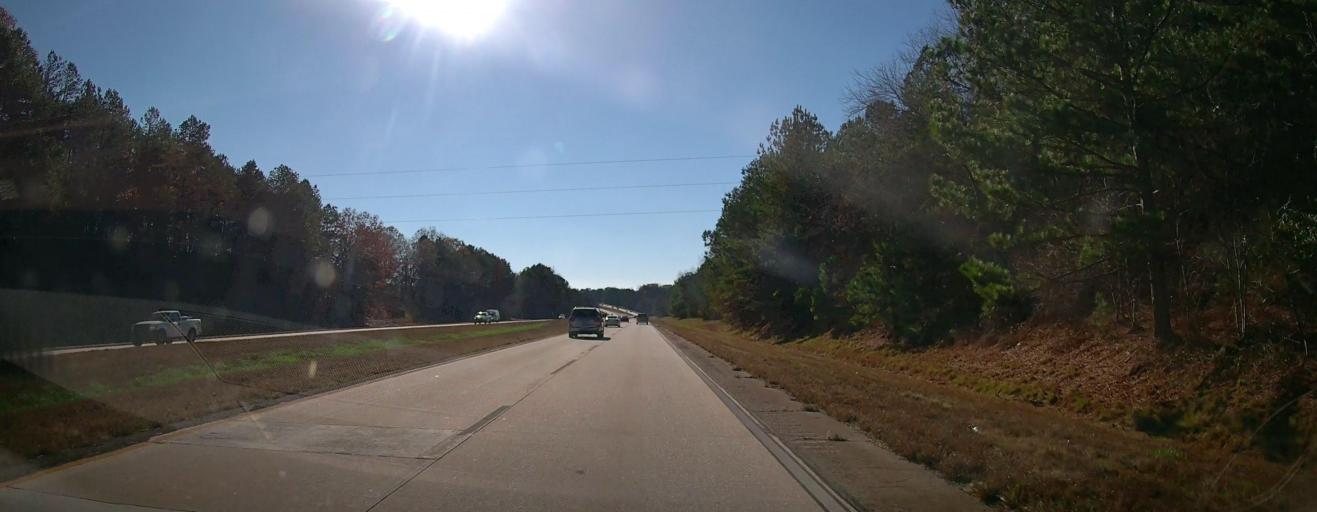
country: US
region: Georgia
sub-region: Hall County
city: Lula
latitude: 34.3910
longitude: -83.6986
